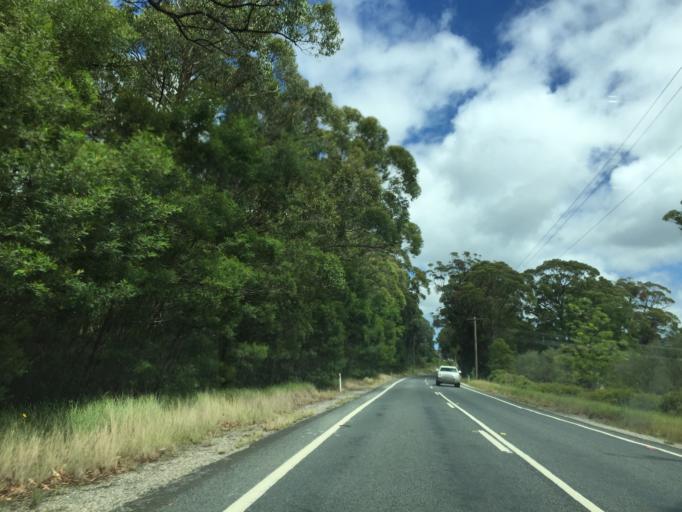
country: AU
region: New South Wales
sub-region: Hawkesbury
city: Richmond
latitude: -33.5164
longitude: 150.5883
